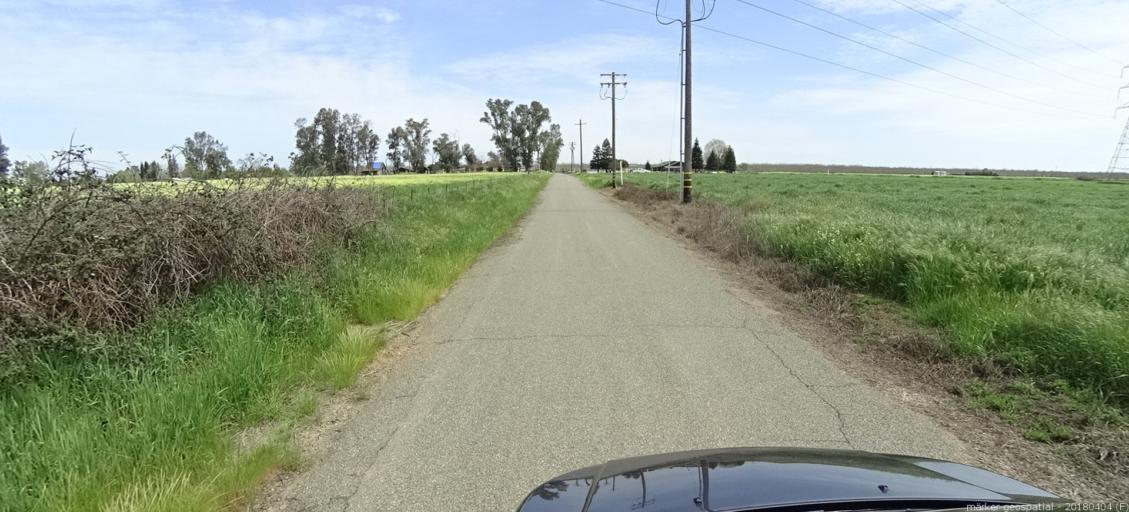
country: US
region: California
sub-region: Sacramento County
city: Herald
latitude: 38.3032
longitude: -121.2241
